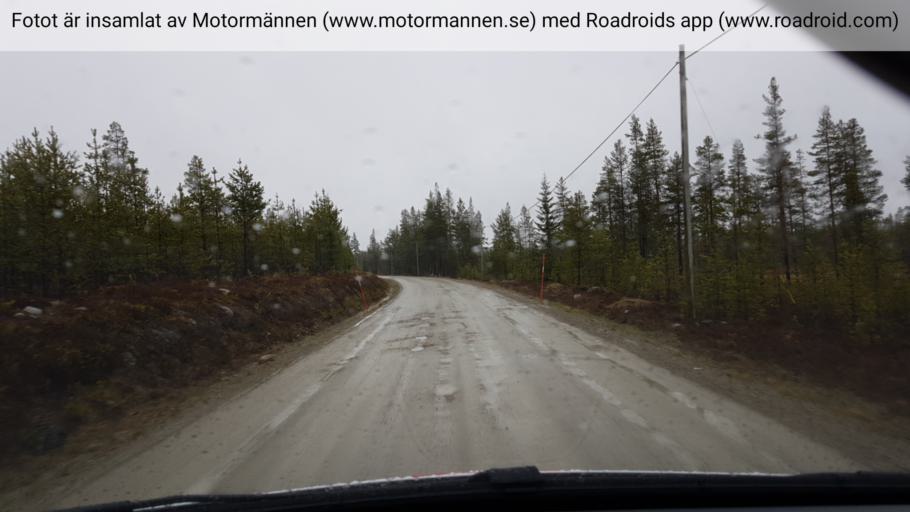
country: SE
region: Jaemtland
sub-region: Are Kommun
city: Jarpen
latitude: 62.5364
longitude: 13.4770
